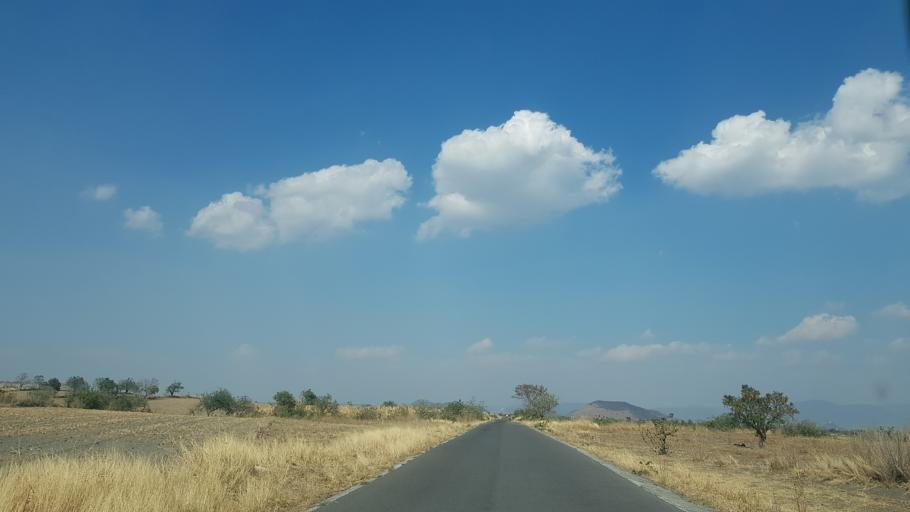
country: MX
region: Puebla
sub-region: Atlixco
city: Colonia Agricola de Ocotepec (Colonia San Jose)
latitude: 18.9195
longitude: -98.5199
